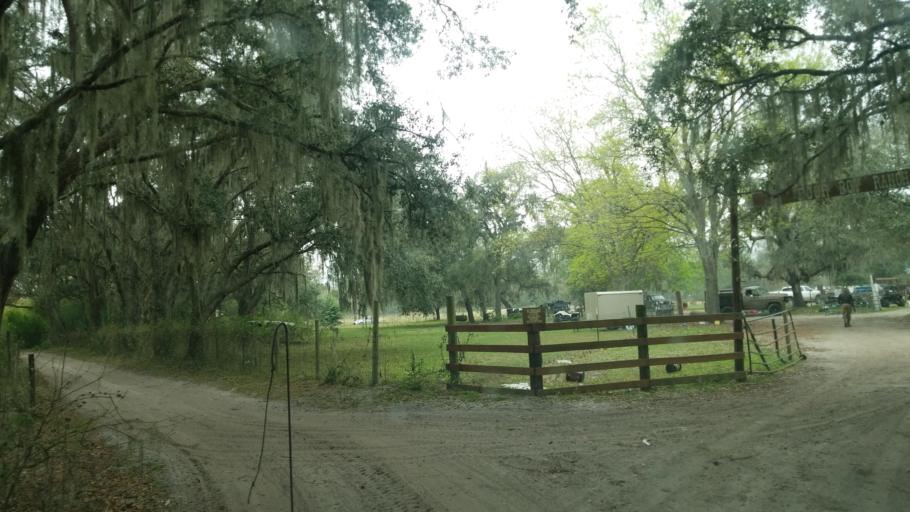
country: US
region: Florida
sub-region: Lake County
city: Groveland
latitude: 28.3837
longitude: -81.8537
